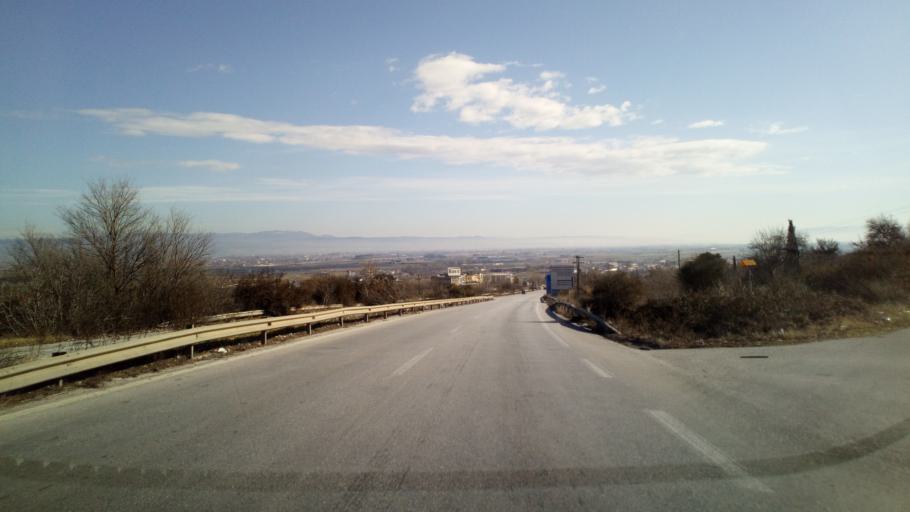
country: GR
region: Central Macedonia
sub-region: Nomos Thessalonikis
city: Lagyna
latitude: 40.7292
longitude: 22.9938
